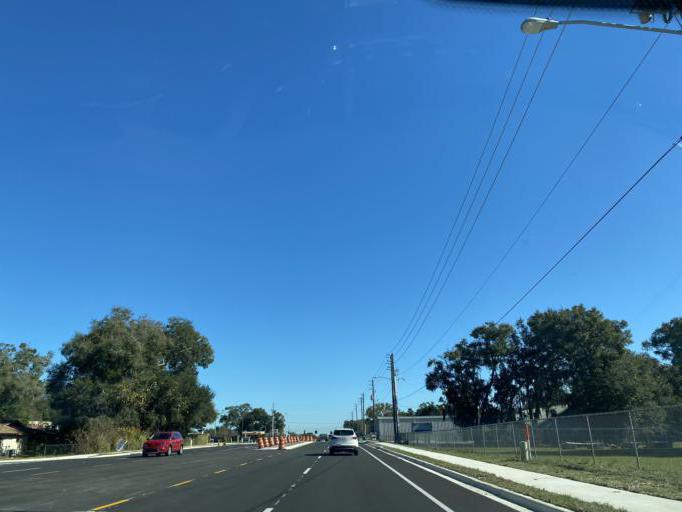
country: US
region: Florida
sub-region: Lake County
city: Fruitland Park
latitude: 28.8613
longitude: -81.9095
